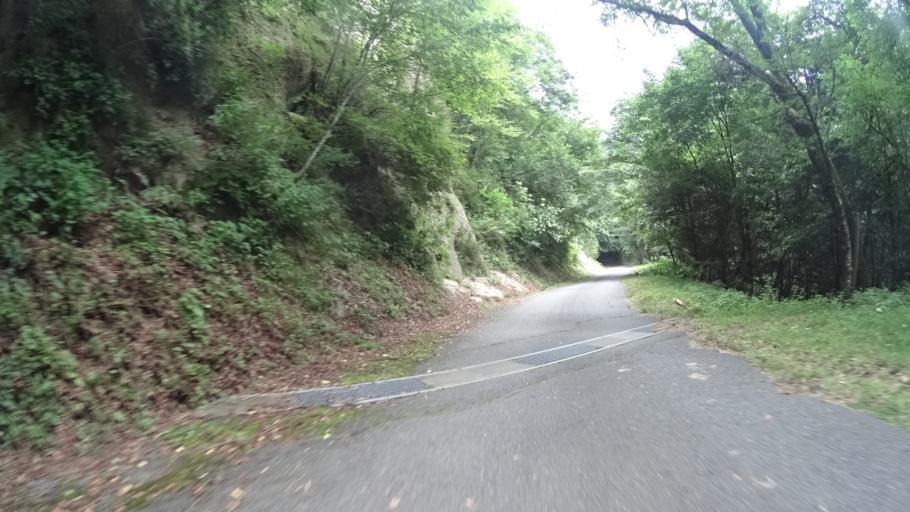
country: JP
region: Yamanashi
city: Kofu-shi
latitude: 35.8243
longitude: 138.5958
